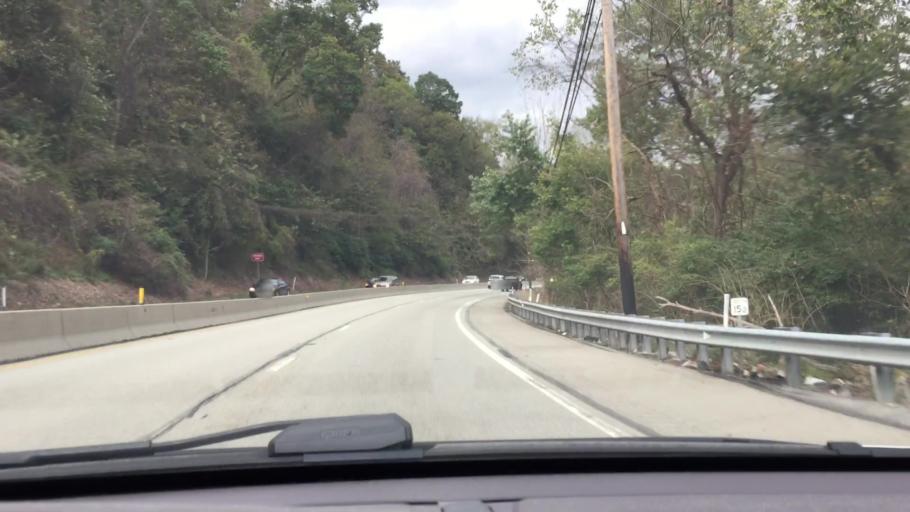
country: US
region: Pennsylvania
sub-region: Allegheny County
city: Jefferson Hills
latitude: 40.2839
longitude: -79.9111
